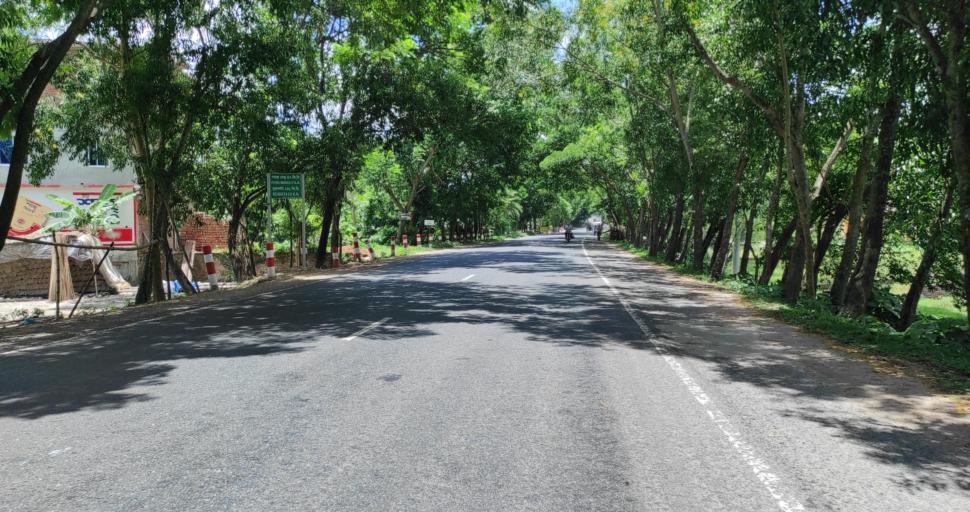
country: BD
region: Barisal
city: Gaurnadi
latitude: 22.8295
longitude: 90.2582
